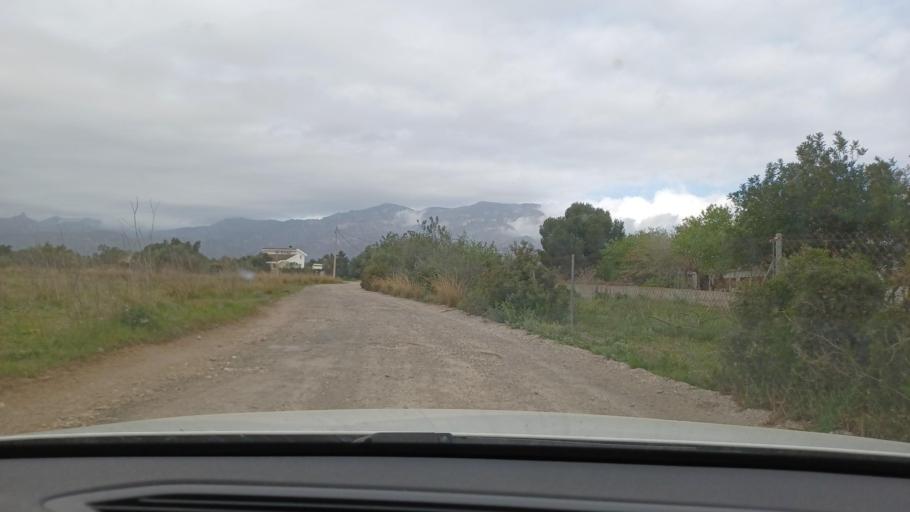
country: ES
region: Catalonia
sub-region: Provincia de Tarragona
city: Tortosa
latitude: 40.7921
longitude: 0.4662
